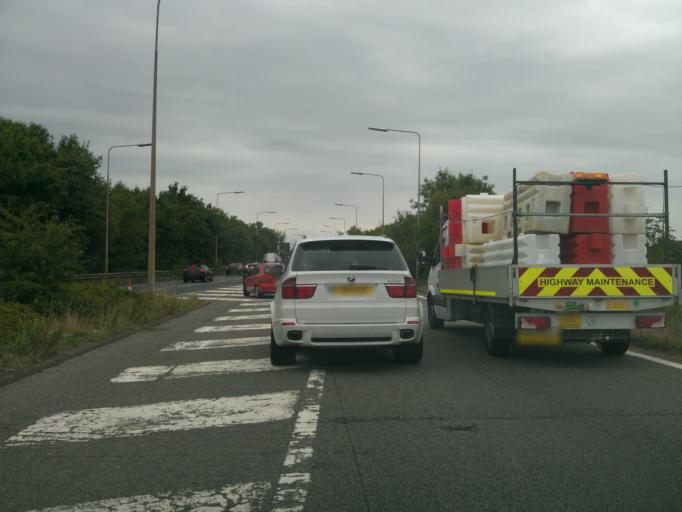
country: GB
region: England
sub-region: Kent
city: West Thurrock
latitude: 51.4915
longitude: 0.2677
